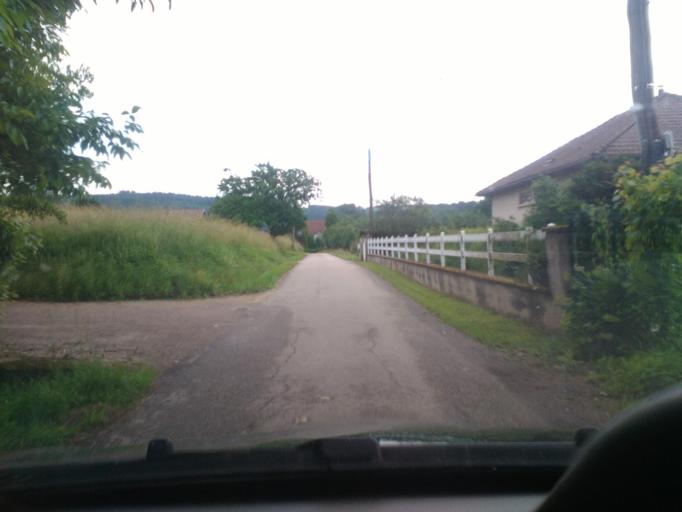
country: FR
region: Lorraine
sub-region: Departement des Vosges
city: Moyenmoutier
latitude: 48.3481
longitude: 6.9257
